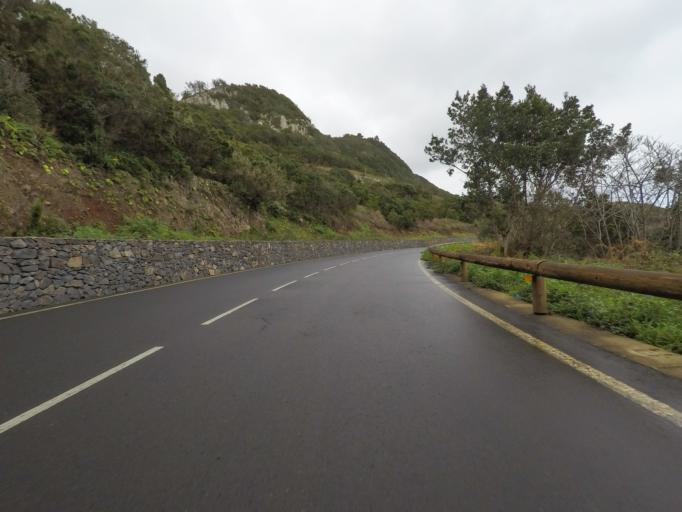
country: ES
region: Canary Islands
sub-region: Provincia de Santa Cruz de Tenerife
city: Agulo
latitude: 28.1892
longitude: -17.2231
